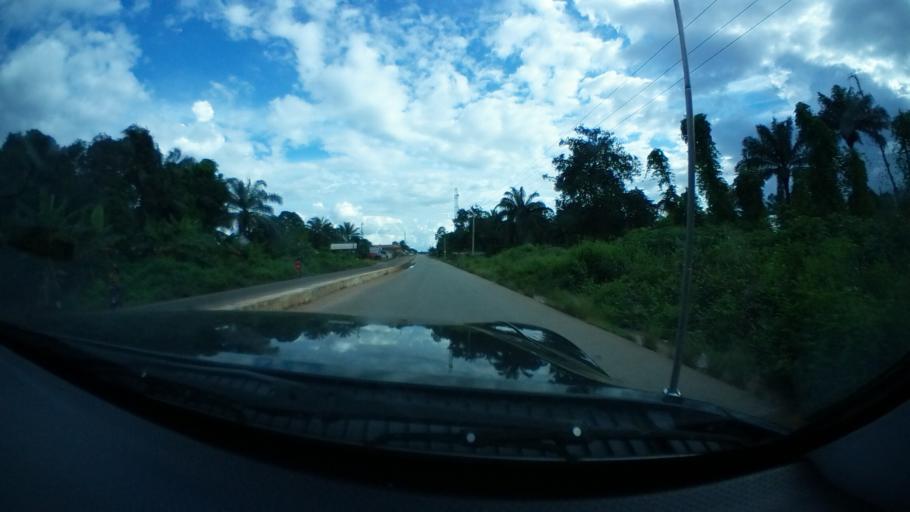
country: NG
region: Anambra
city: Uga
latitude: 5.8644
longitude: 7.1019
